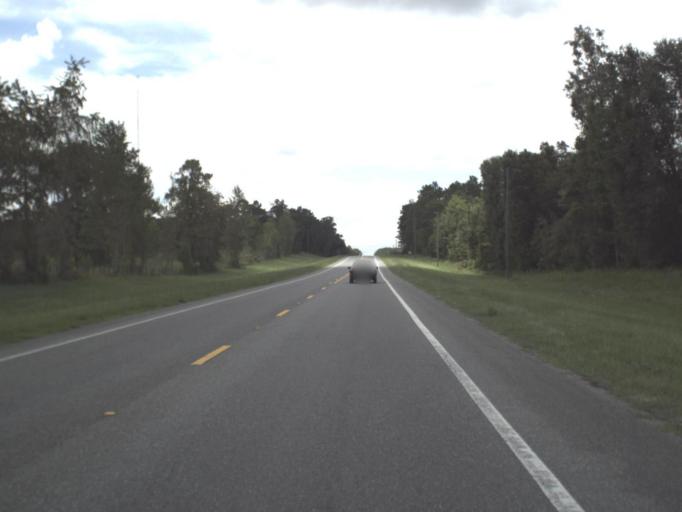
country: US
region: Florida
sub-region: Suwannee County
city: Live Oak
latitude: 30.2118
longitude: -82.9880
